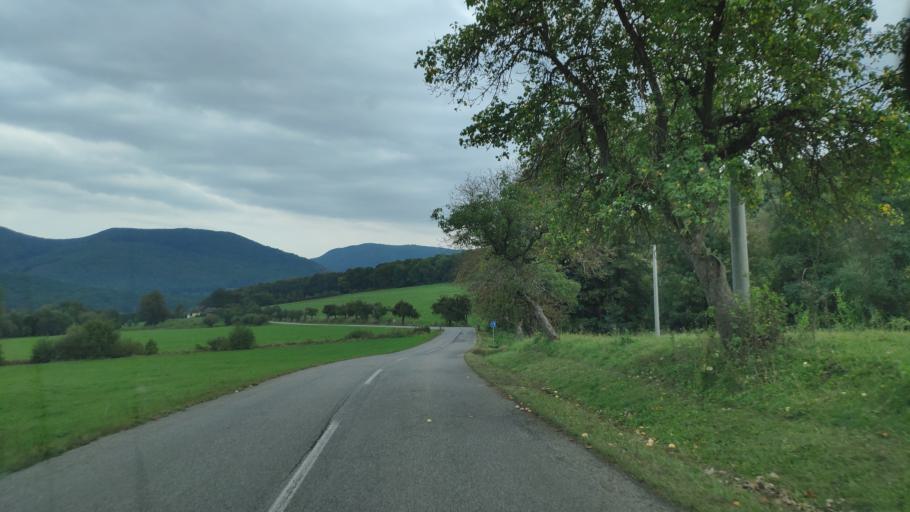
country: SK
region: Kosicky
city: Dobsina
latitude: 48.6792
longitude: 20.3375
